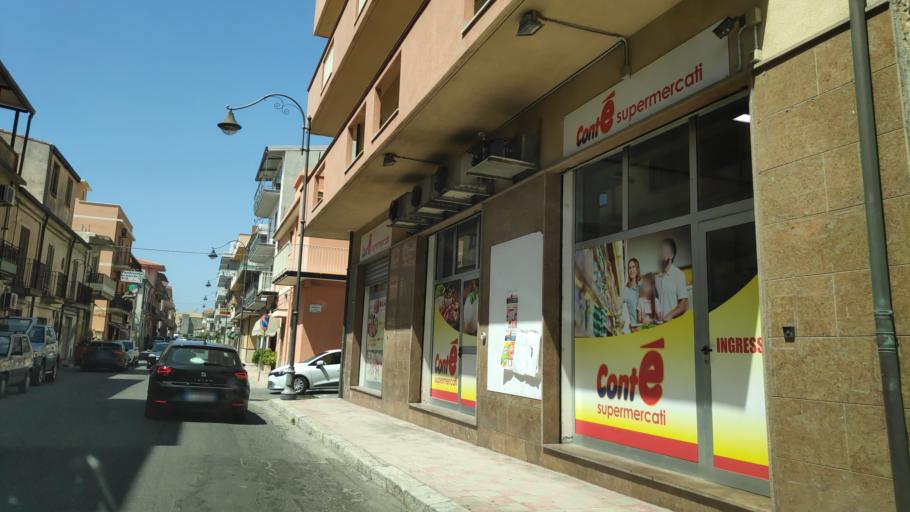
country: IT
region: Calabria
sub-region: Provincia di Reggio Calabria
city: Bova Marina
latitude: 37.9305
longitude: 15.9187
